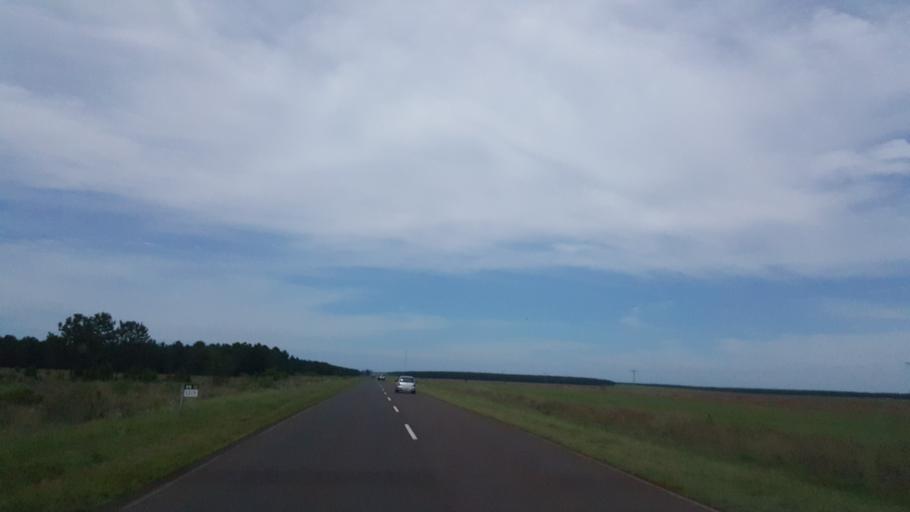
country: PY
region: Itapua
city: San Juan del Parana
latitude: -27.5100
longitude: -56.1343
